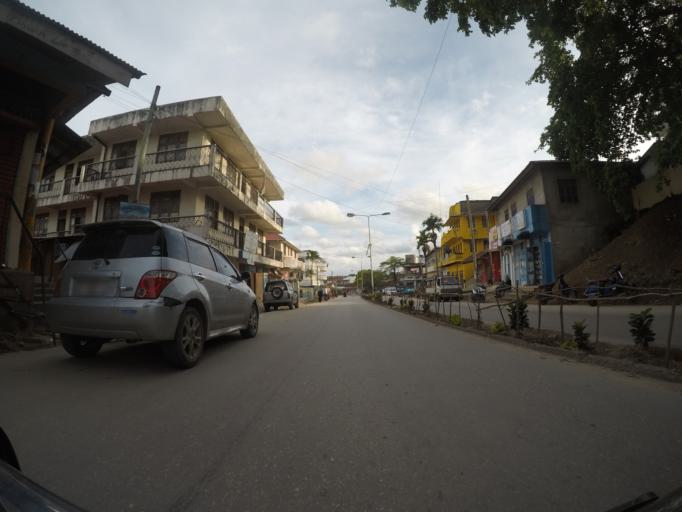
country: TZ
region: Pemba South
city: Chake Chake
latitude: -5.2450
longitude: 39.7680
